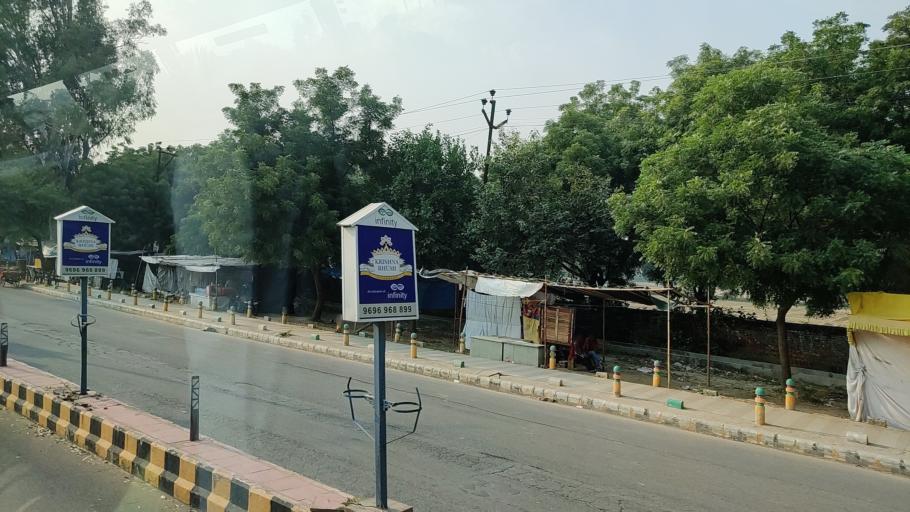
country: IN
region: Uttar Pradesh
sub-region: Mathura
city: Vrindavan
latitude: 27.5630
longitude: 77.6350
